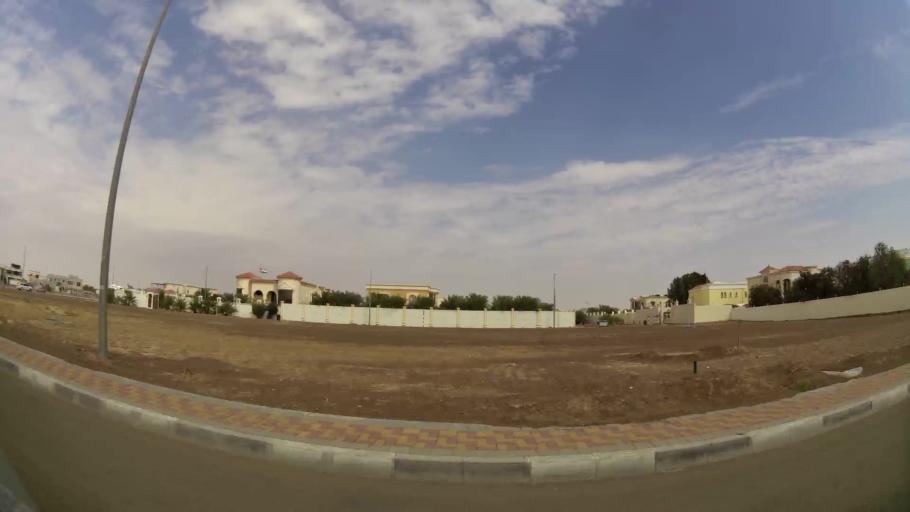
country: AE
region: Abu Dhabi
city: Al Ain
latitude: 24.1971
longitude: 55.8016
